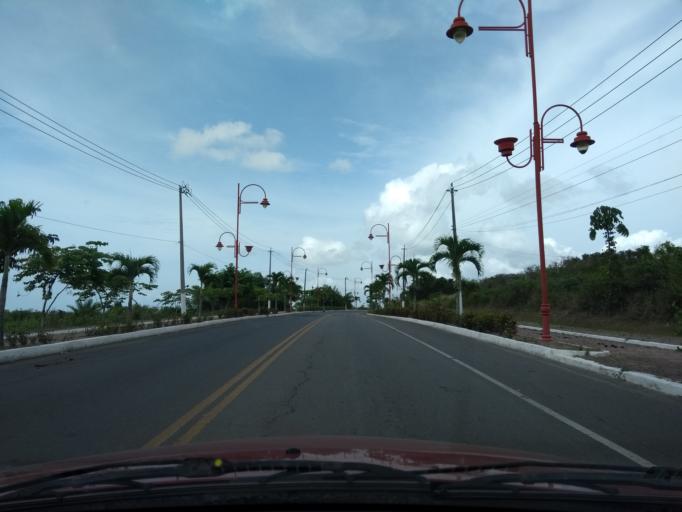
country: BR
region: Bahia
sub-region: Sao Francisco Do Conde
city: Sao Francisco do Conde
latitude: -12.6143
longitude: -38.6565
